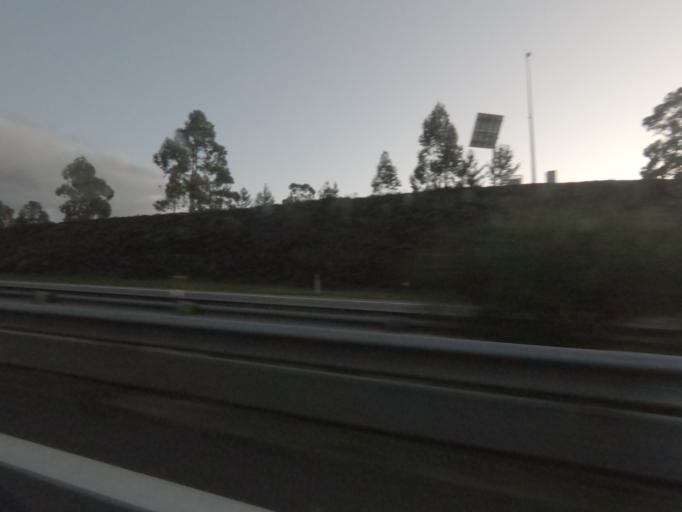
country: PT
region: Porto
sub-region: Paredes
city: Recarei
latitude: 41.1658
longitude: -8.4023
